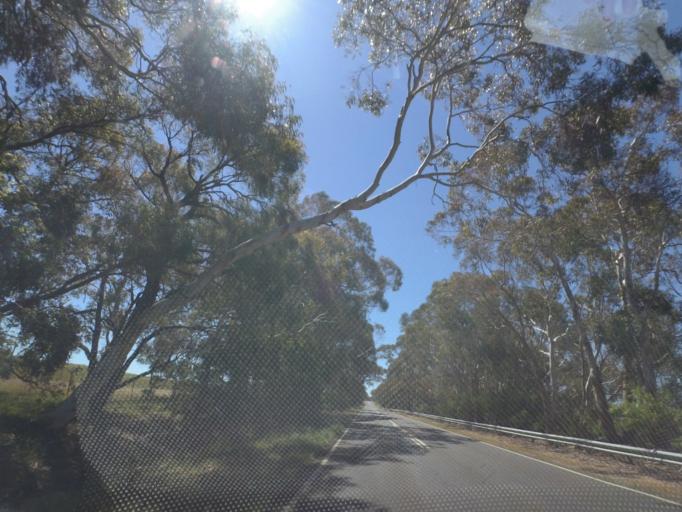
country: AU
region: Victoria
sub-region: Hume
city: Sunbury
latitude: -37.1371
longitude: 144.7683
